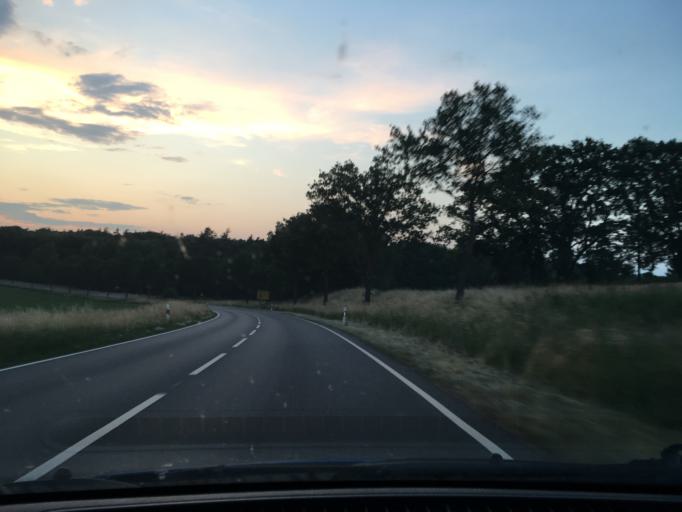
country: DE
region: Lower Saxony
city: Bad Bevensen
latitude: 53.0781
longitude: 10.5608
